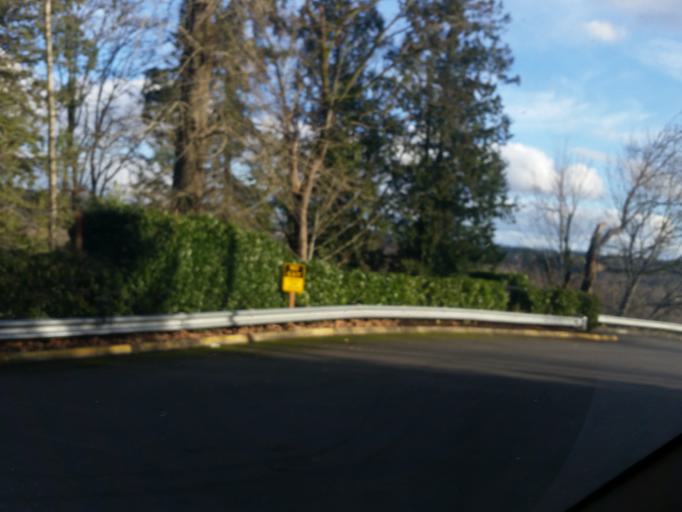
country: US
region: Washington
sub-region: King County
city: Kingsgate
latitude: 47.7151
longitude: -122.1553
